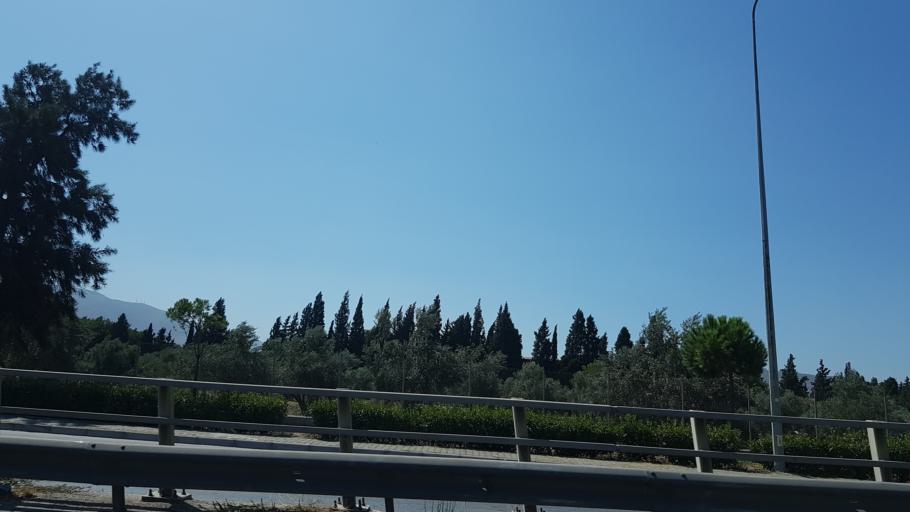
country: TR
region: Izmir
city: Bornova
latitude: 38.4593
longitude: 27.2195
